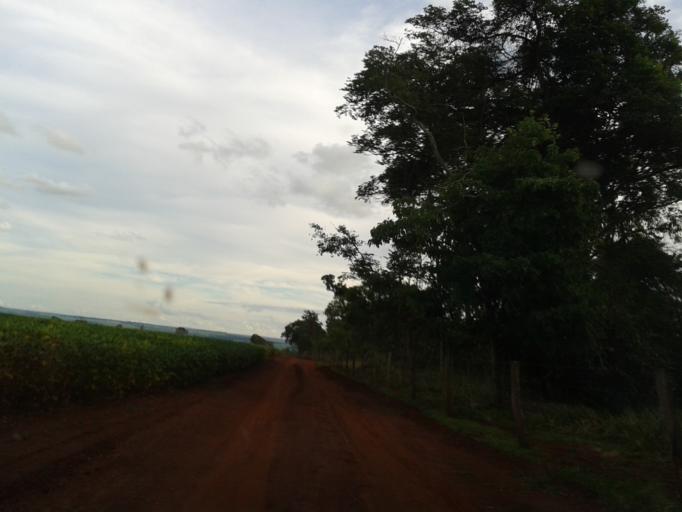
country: BR
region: Minas Gerais
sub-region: Capinopolis
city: Capinopolis
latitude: -18.7500
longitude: -49.8114
